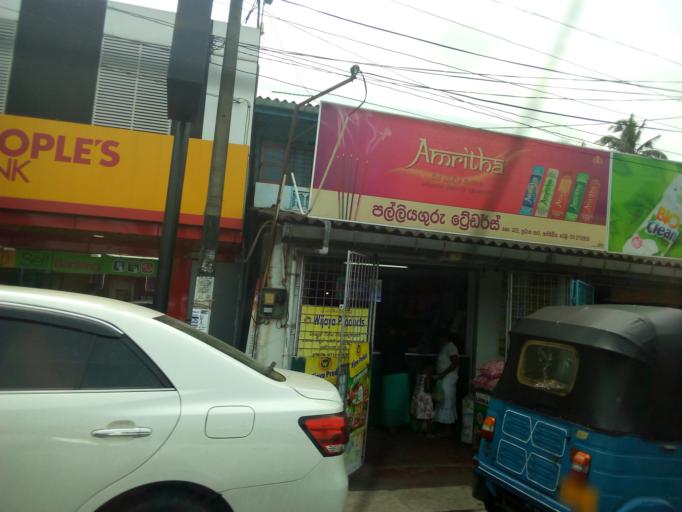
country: LK
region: Western
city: Galkissa
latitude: 6.8395
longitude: 79.8848
